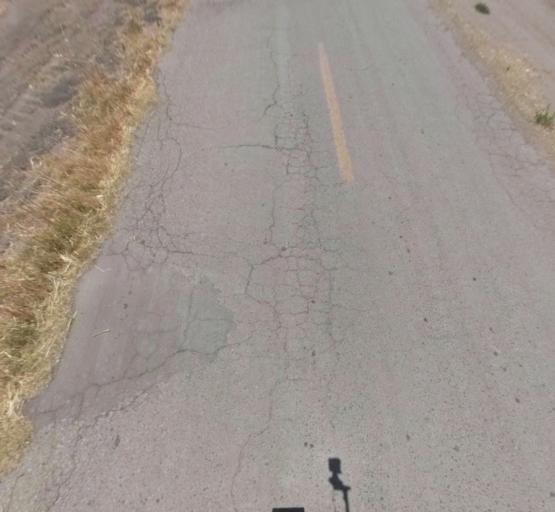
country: US
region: California
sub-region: Merced County
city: Dos Palos
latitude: 37.0477
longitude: -120.5286
